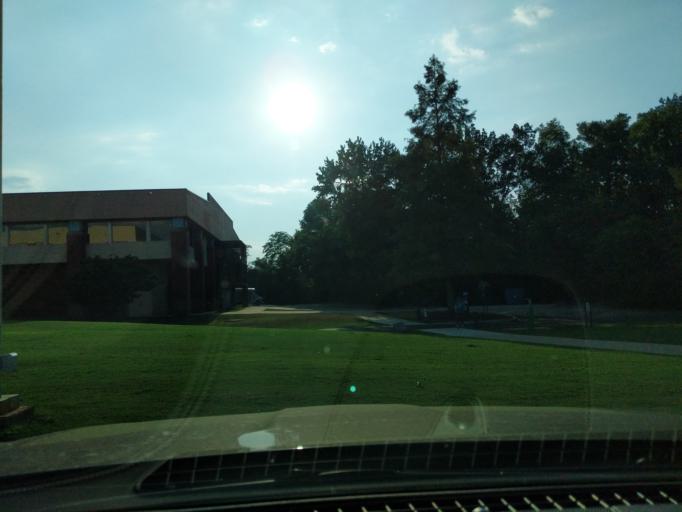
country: US
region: South Carolina
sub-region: Aiken County
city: North Augusta
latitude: 33.4997
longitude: -81.9876
